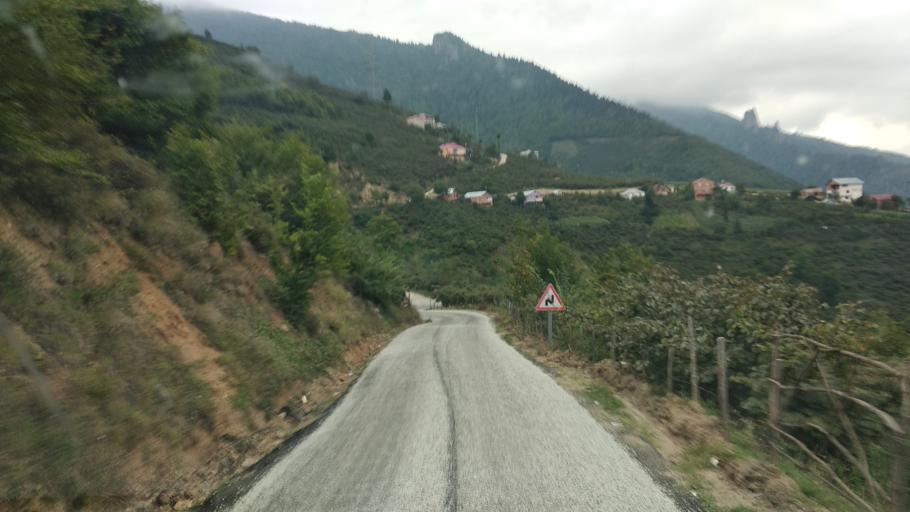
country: TR
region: Giresun
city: Dogankent
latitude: 40.7429
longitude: 38.9925
